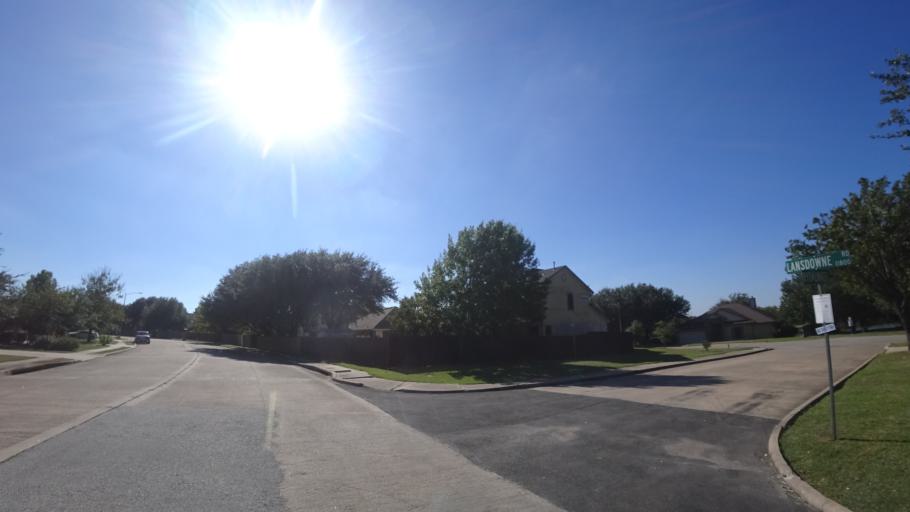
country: US
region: Texas
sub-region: Travis County
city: Manor
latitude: 30.3569
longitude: -97.6124
